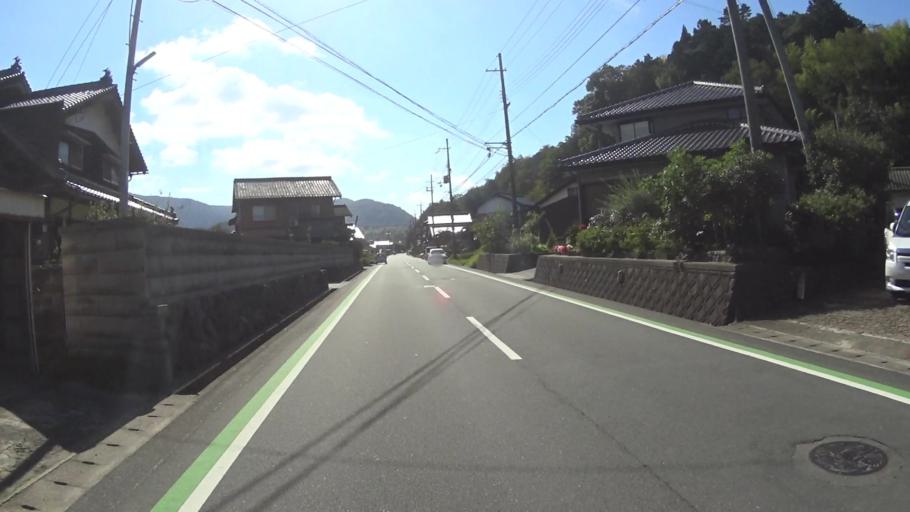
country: JP
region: Kyoto
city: Miyazu
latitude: 35.6570
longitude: 135.0886
